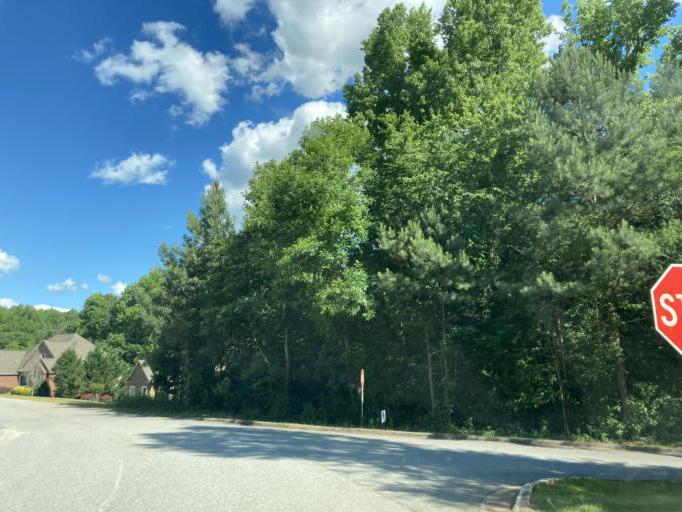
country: US
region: Georgia
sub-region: Jones County
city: Gray
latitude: 32.9949
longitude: -83.5495
